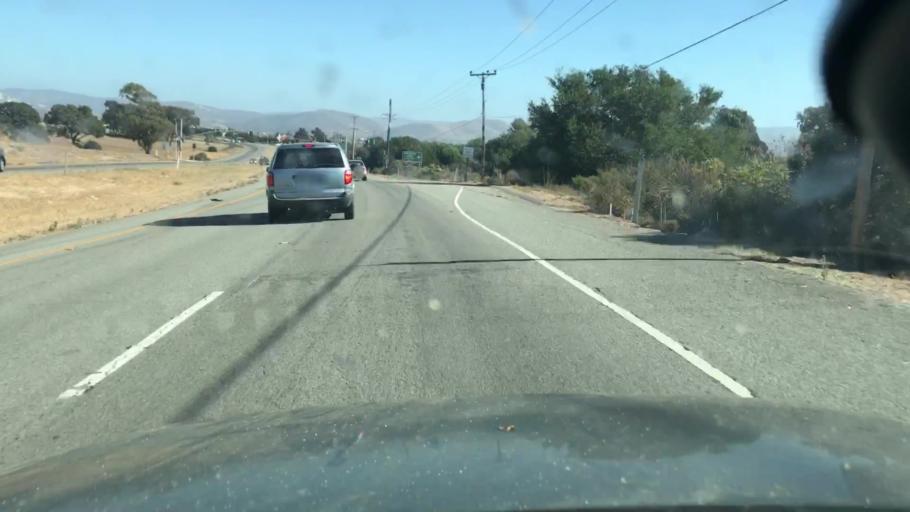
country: US
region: California
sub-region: Santa Barbara County
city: Mission Hills
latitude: 34.6832
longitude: -120.4595
